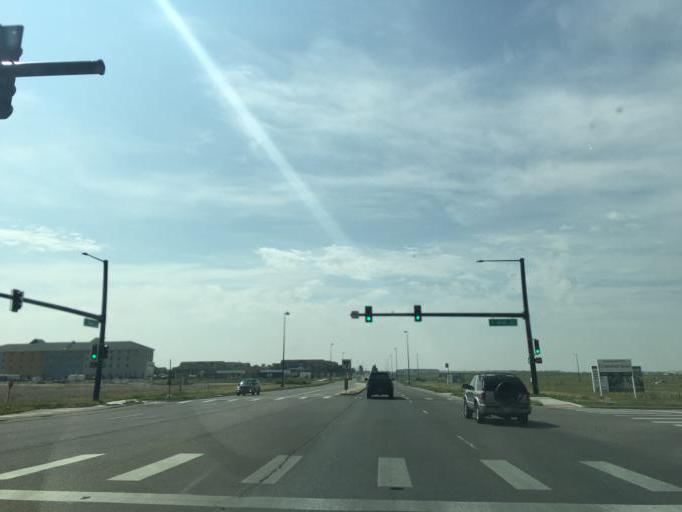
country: US
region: Colorado
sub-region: Adams County
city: Aurora
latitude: 39.8078
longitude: -104.7722
